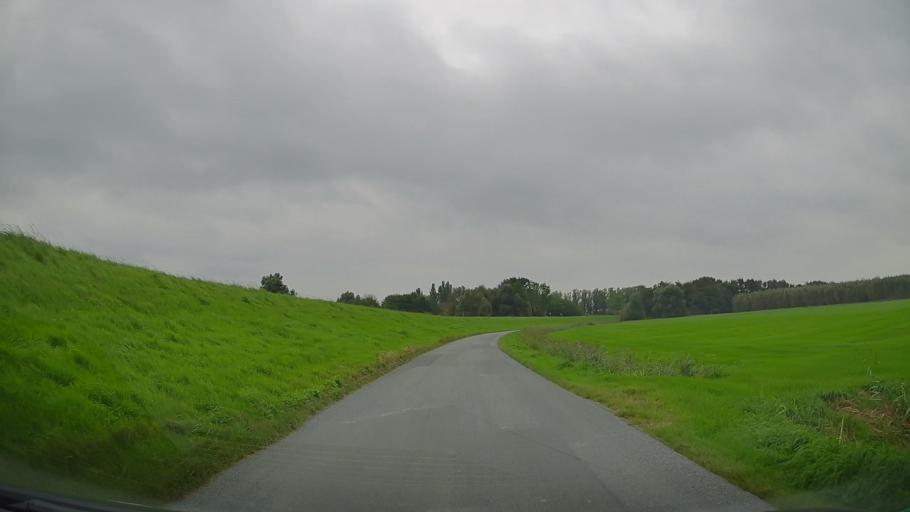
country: DE
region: Lower Saxony
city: Neuhaus an der Oste
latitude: 53.8097
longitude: 9.0356
